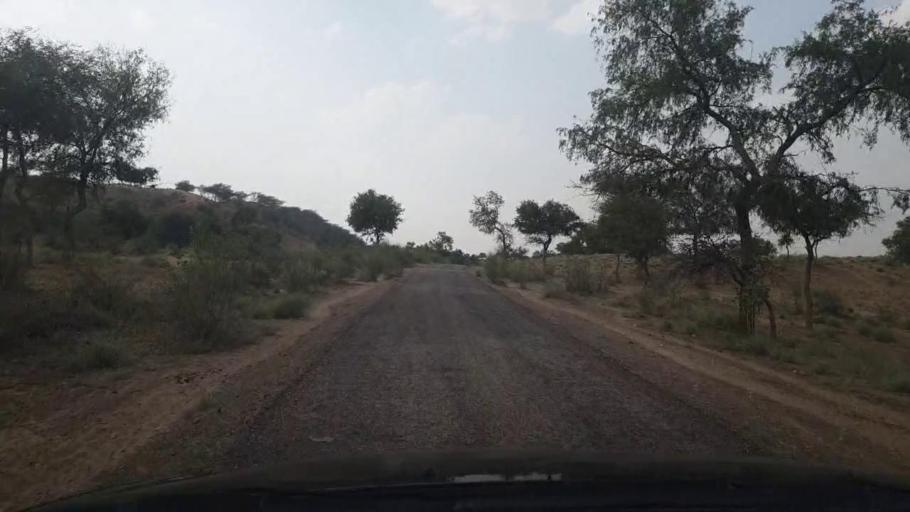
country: PK
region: Sindh
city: Islamkot
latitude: 24.9660
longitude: 70.6036
